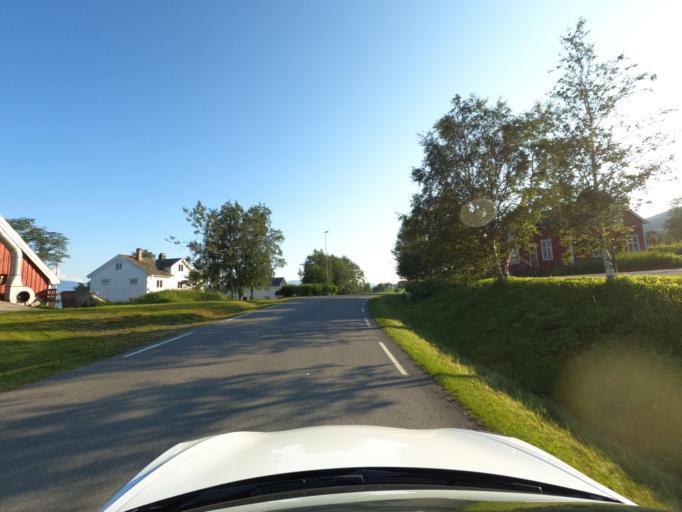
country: NO
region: Nordland
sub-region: Evenes
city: Randa
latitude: 68.4749
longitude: 16.8823
